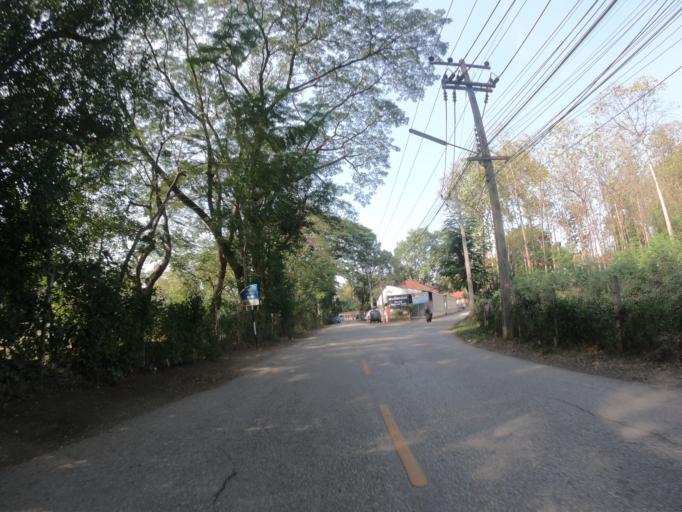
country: TH
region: Chiang Mai
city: Chiang Mai
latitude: 18.7731
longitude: 99.0112
